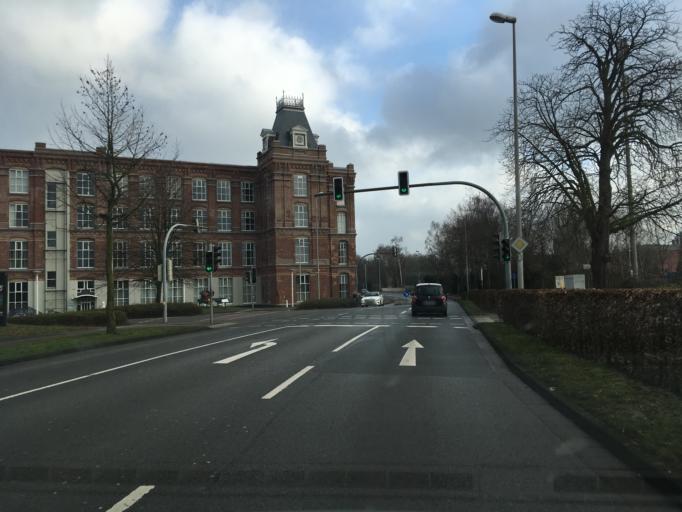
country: DE
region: North Rhine-Westphalia
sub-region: Regierungsbezirk Munster
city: Gronau
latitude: 52.2155
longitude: 7.0232
